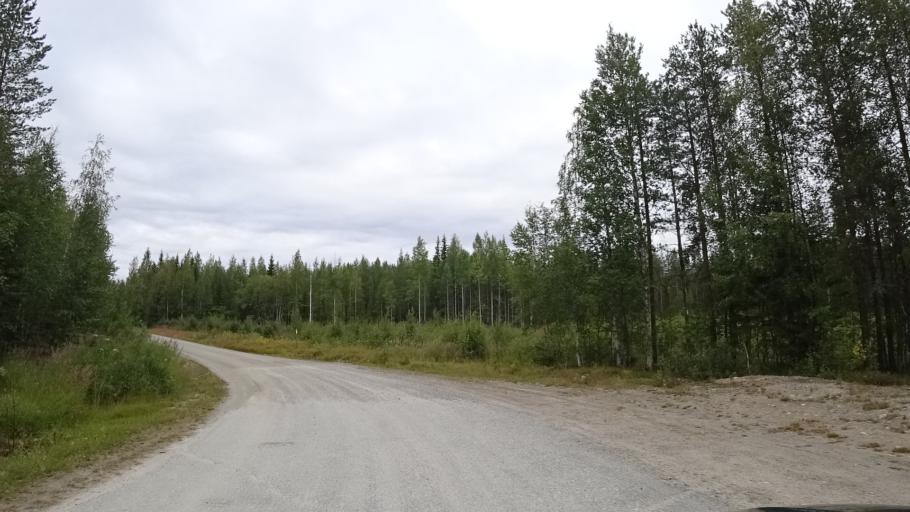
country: FI
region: North Karelia
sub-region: Joensuu
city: Ilomantsi
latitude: 63.1539
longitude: 30.6221
